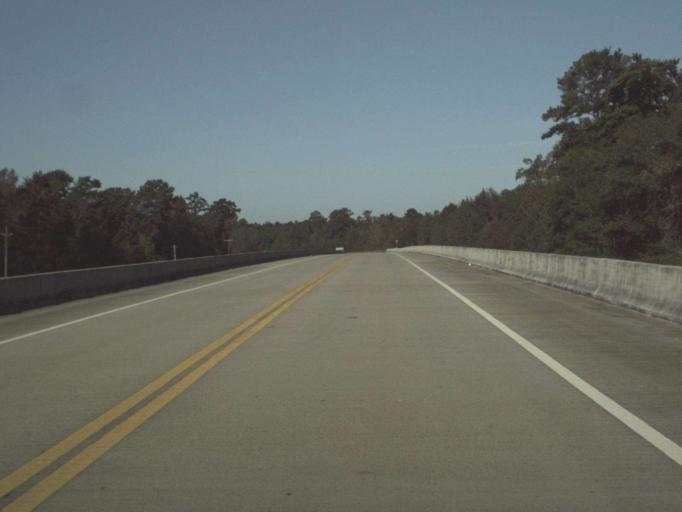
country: US
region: Florida
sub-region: Holmes County
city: Bonifay
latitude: 30.7765
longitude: -85.8286
